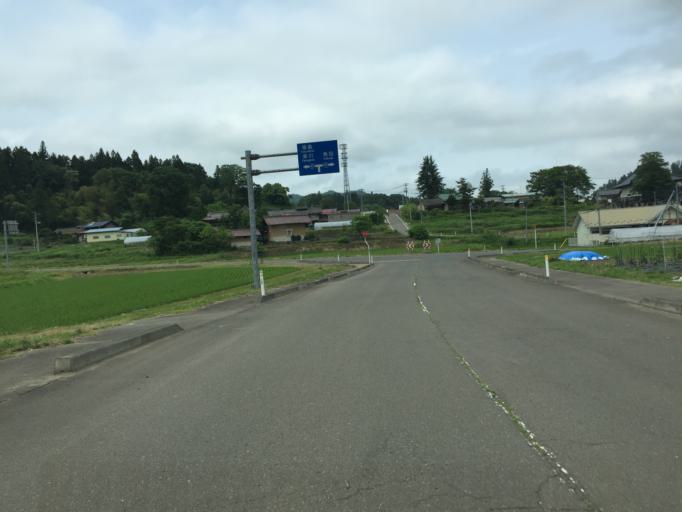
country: JP
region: Miyagi
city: Marumori
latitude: 37.8252
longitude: 140.7273
